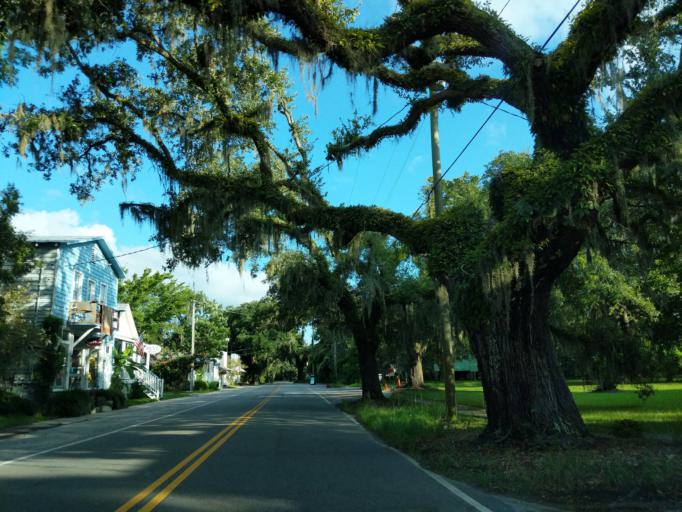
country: US
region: South Carolina
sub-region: Charleston County
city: Awendaw
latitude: 33.0906
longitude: -79.4630
